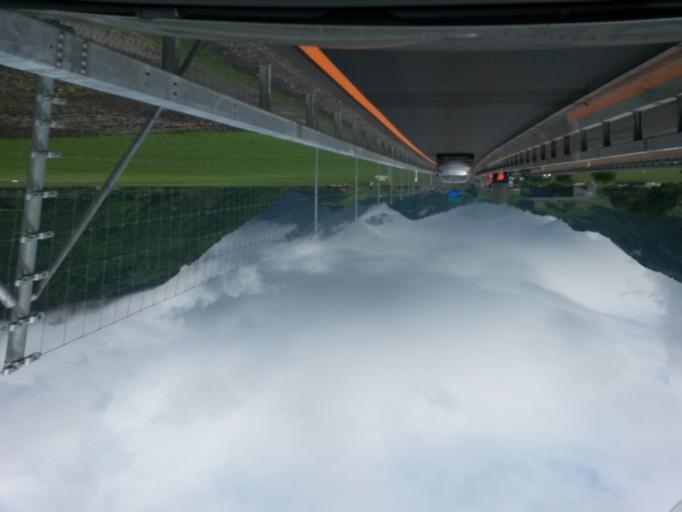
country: CH
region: Nidwalden
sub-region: Nidwalden
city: Ennetburgen
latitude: 46.9695
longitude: 8.3977
